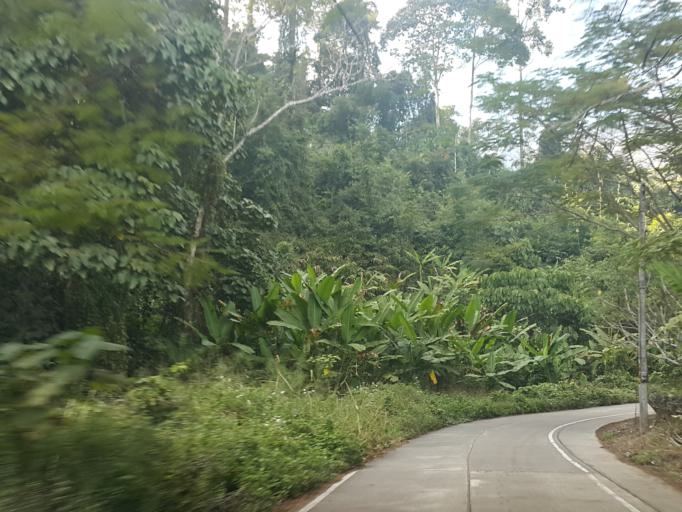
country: TH
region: Chiang Mai
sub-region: Amphoe Chiang Dao
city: Chiang Dao
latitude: 19.4110
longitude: 98.9219
